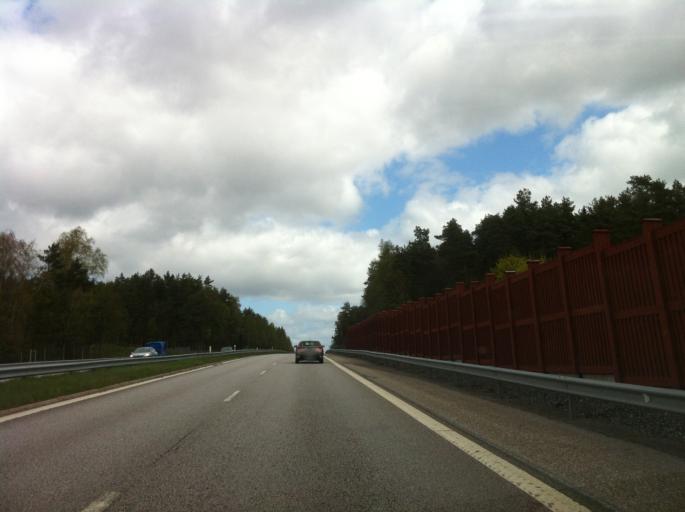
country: SE
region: Vaestra Goetaland
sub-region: Alingsas Kommun
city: Ingared
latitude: 57.8545
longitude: 12.4752
